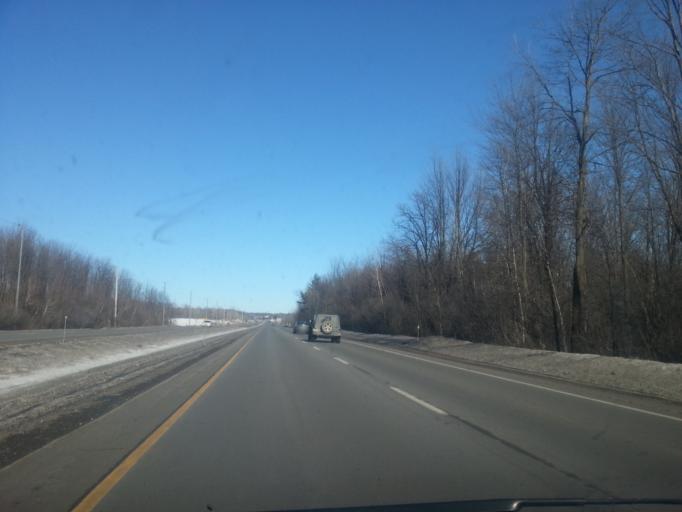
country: CA
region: Ontario
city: Ottawa
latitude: 45.4276
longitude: -75.5612
